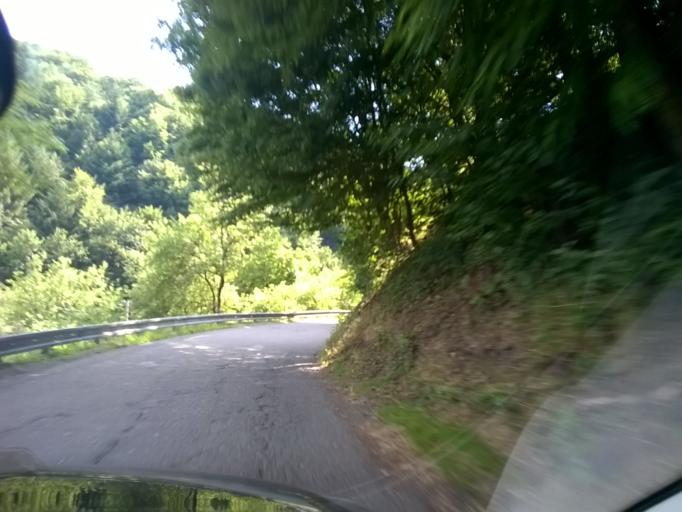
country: SK
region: Banskobystricky
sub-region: Okres Banska Bystrica
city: Banska Stiavnica
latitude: 48.4680
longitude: 18.8420
